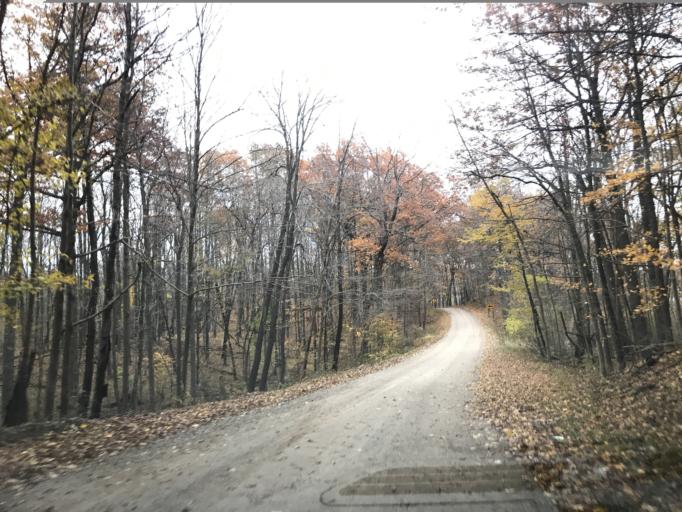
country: US
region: Michigan
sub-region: Lenawee County
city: Manitou Beach-Devils Lake
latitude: 42.0258
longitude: -84.3350
